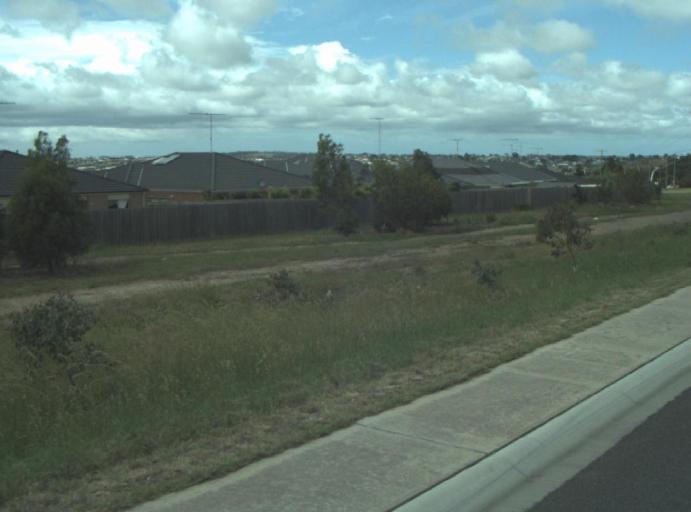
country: AU
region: Victoria
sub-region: Greater Geelong
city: Wandana Heights
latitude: -38.1906
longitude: 144.3066
